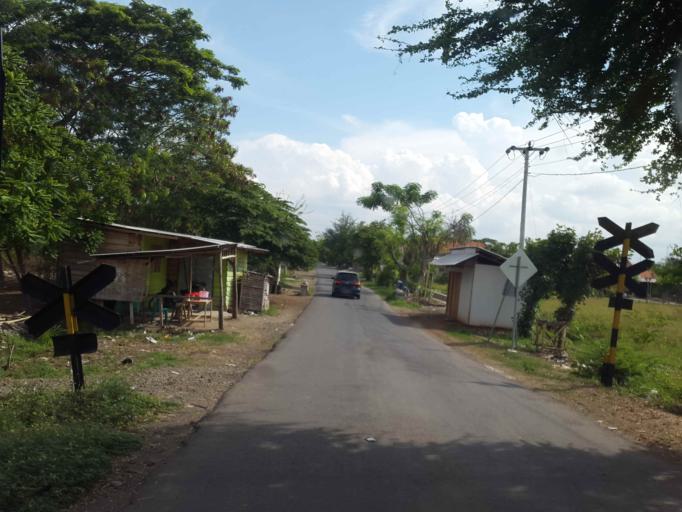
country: ID
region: Central Java
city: Pemalang
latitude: -6.8824
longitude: 109.3273
